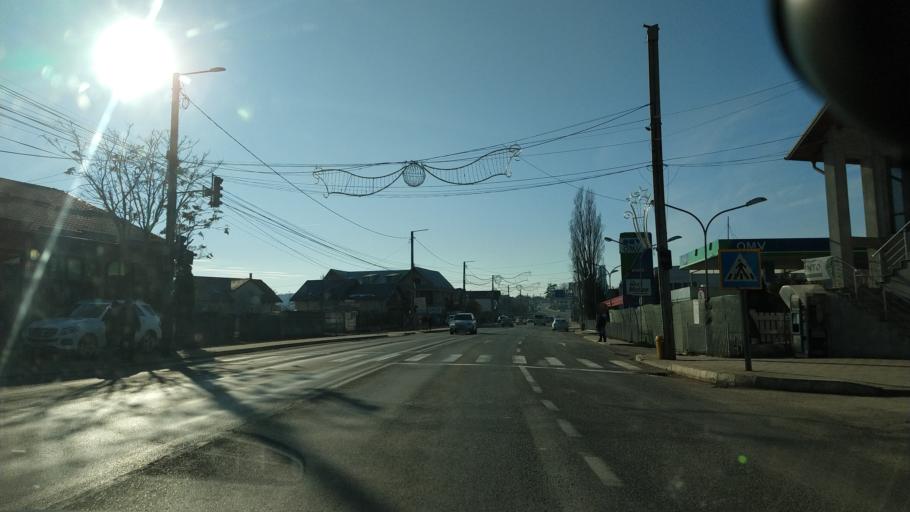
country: RO
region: Iasi
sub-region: Comuna Ion Neculce
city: Buznea
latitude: 47.2066
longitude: 27.0109
